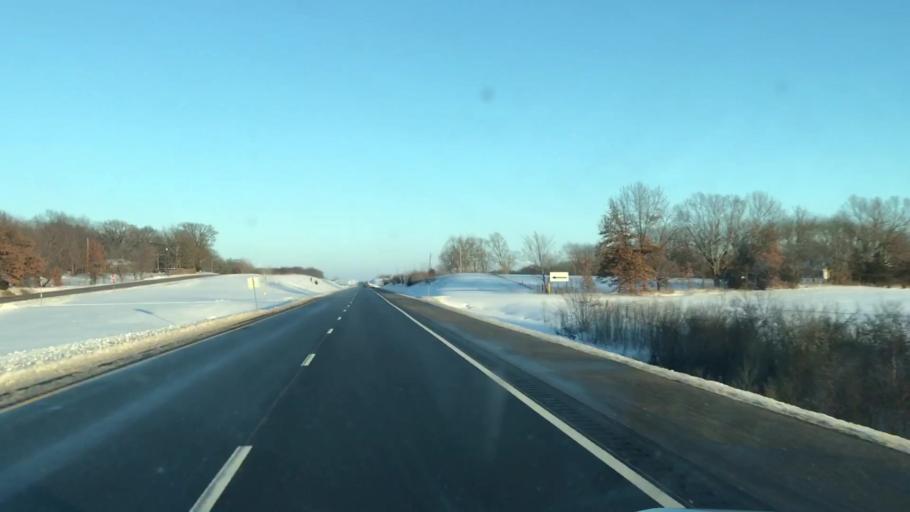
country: US
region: Missouri
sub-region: DeKalb County
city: Maysville
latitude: 39.7620
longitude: -94.4788
